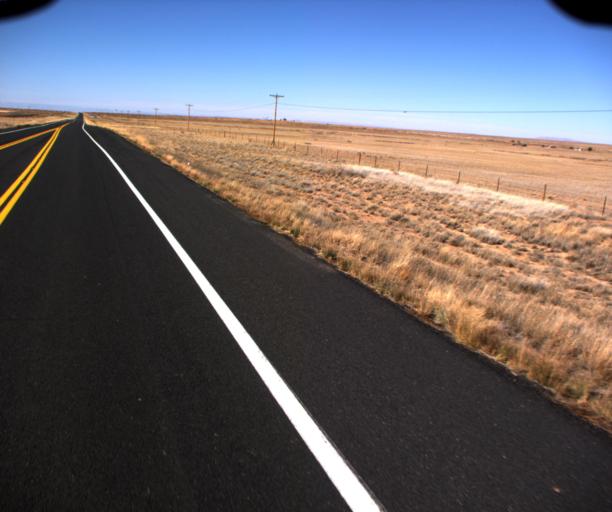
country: US
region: Arizona
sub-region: Coconino County
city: Tuba City
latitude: 35.9985
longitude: -111.0317
